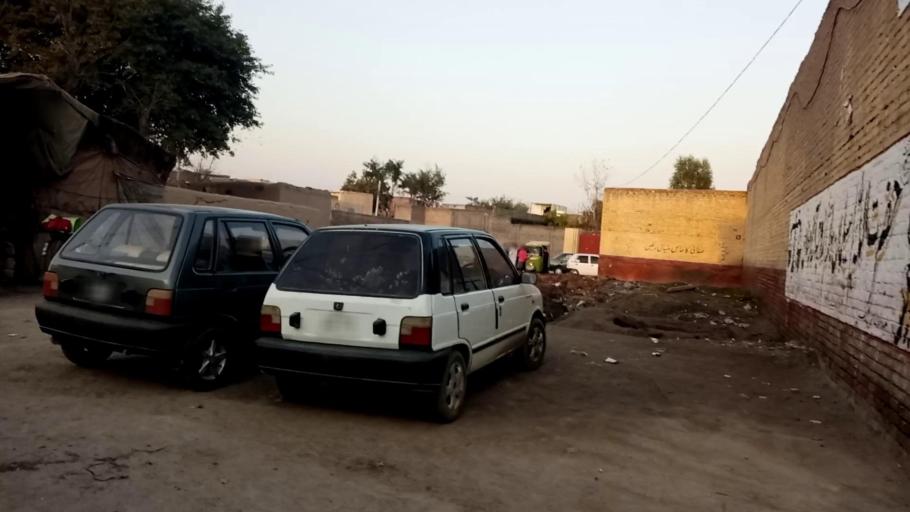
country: PK
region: Khyber Pakhtunkhwa
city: Peshawar
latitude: 34.0511
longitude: 71.4593
